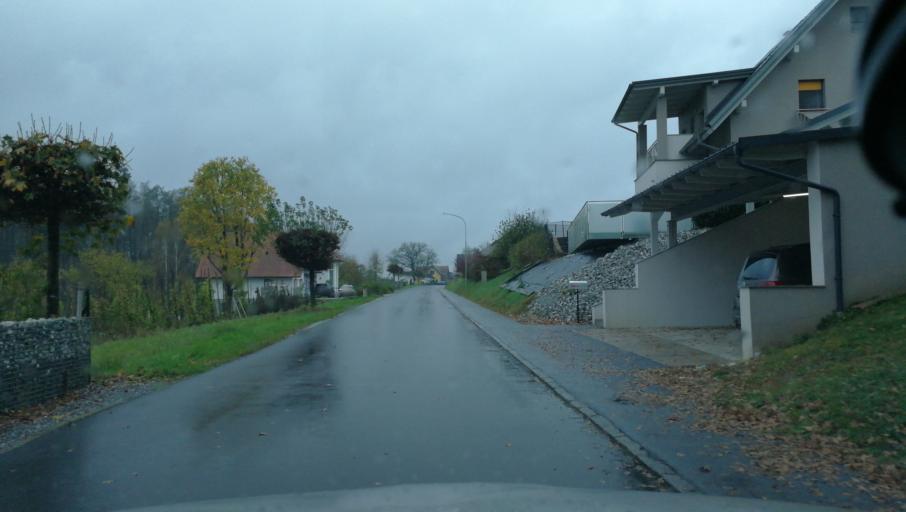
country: AT
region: Styria
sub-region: Politischer Bezirk Leibnitz
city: Strass in Steiermark
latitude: 46.7372
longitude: 15.6469
